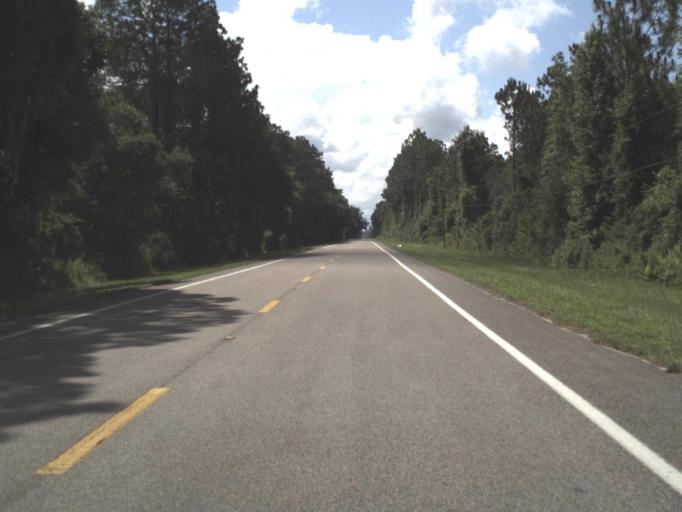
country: US
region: Florida
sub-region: Putnam County
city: Crescent City
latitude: 29.5489
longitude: -81.5306
